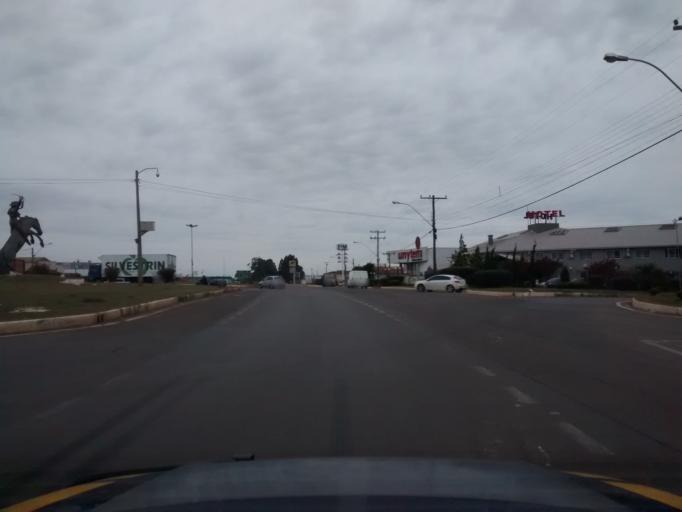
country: BR
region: Rio Grande do Sul
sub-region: Vacaria
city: Vacaria
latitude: -28.5013
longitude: -50.9203
